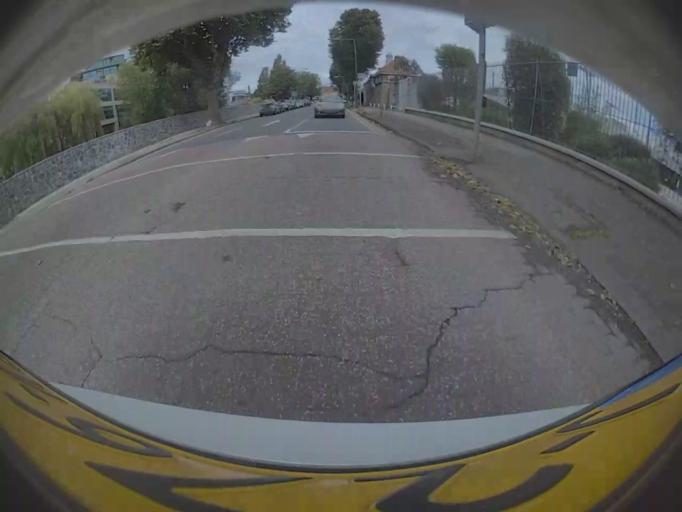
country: IE
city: Clonskeagh
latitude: 53.3276
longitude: -6.2308
